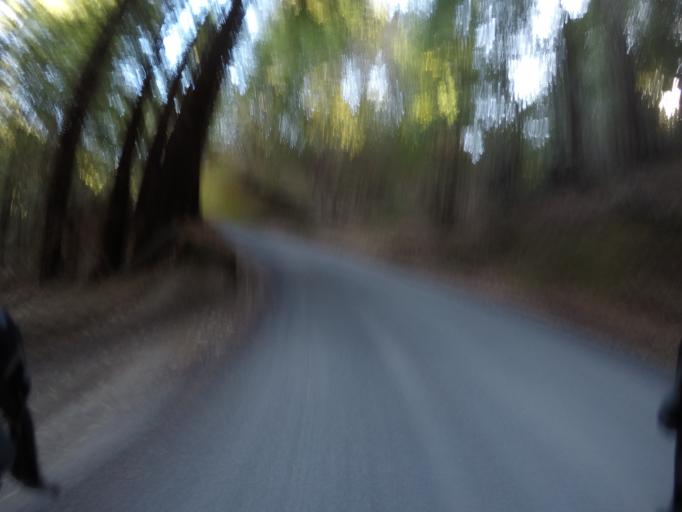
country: US
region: California
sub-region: Santa Cruz County
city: Lompico
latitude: 37.1344
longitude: -122.0209
